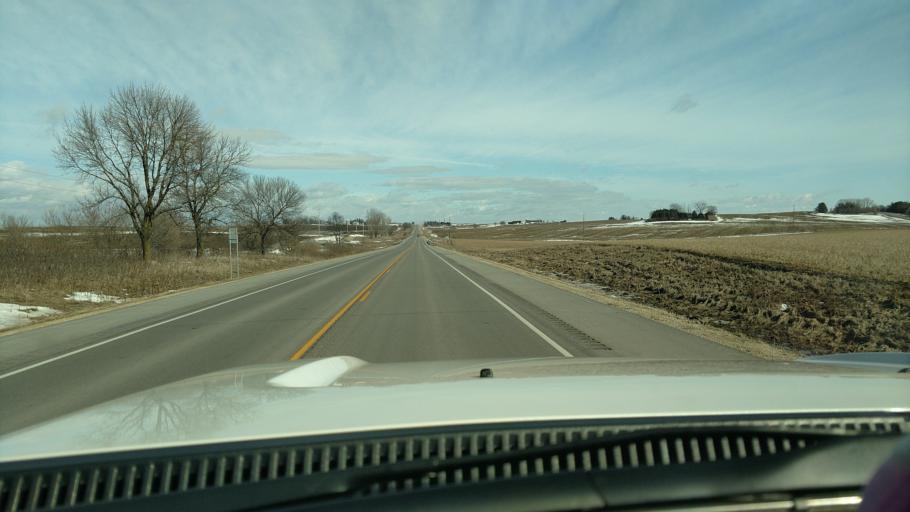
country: US
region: Minnesota
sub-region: Wabasha County
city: Elgin
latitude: 44.1380
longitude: -92.2450
